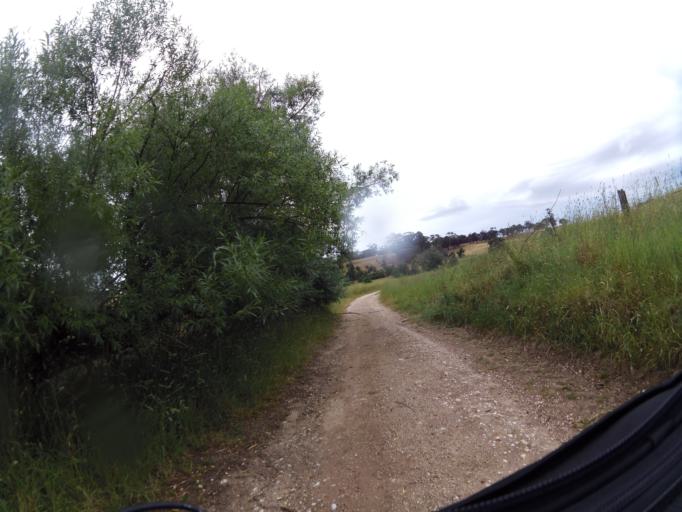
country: AU
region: Victoria
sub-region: Mount Alexander
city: Castlemaine
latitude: -37.2105
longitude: 144.0262
